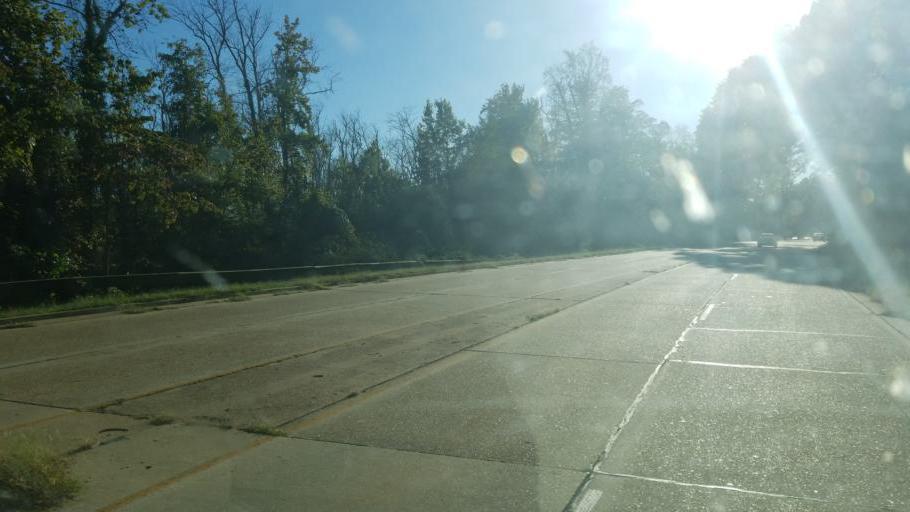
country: US
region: Virginia
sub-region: Fairfax County
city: Fort Hunt
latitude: 38.7109
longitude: -77.0539
